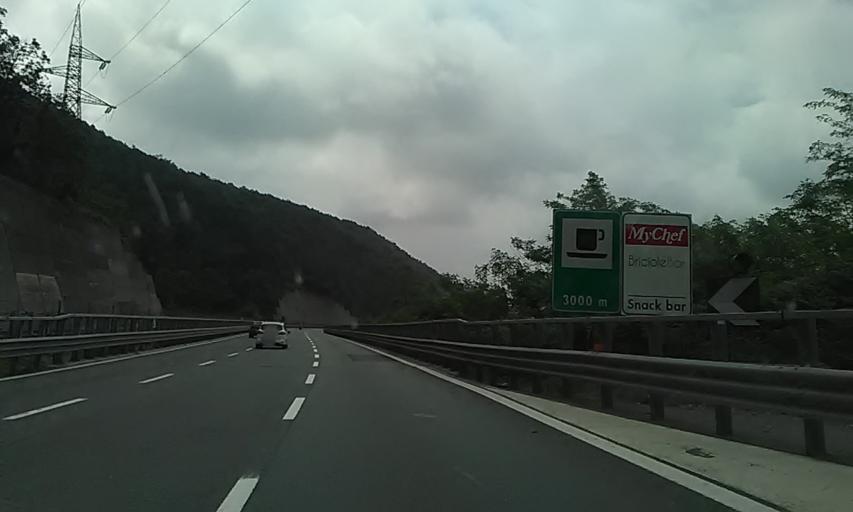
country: IT
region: Liguria
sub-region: Provincia di Genova
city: Masone
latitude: 44.4809
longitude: 8.7340
